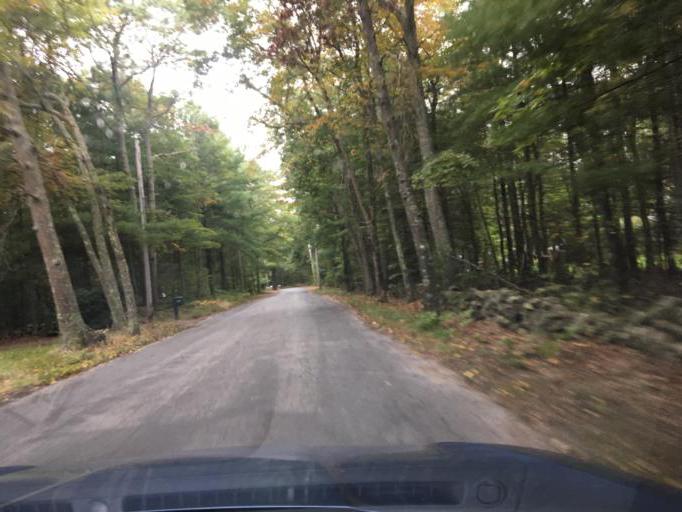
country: US
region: Rhode Island
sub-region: Washington County
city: Exeter
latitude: 41.6015
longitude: -71.5692
